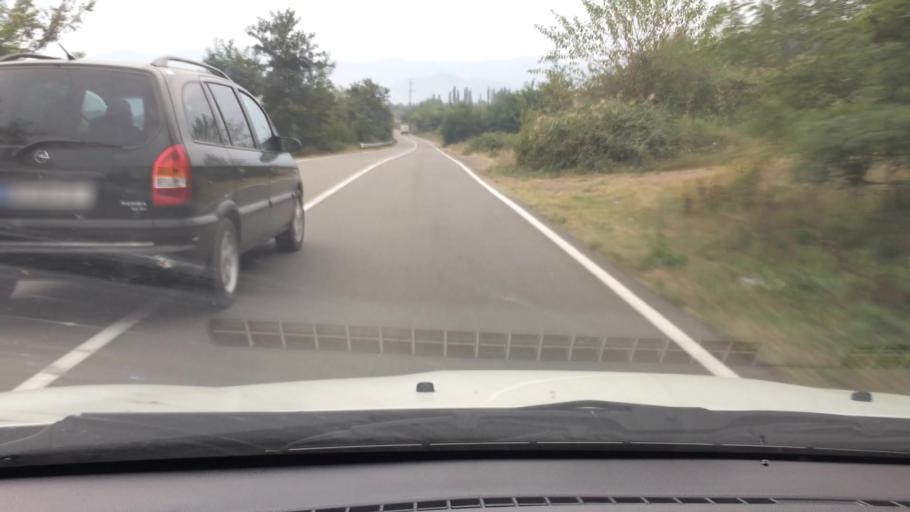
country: AM
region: Tavush
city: Bagratashen
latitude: 41.2720
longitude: 44.7906
